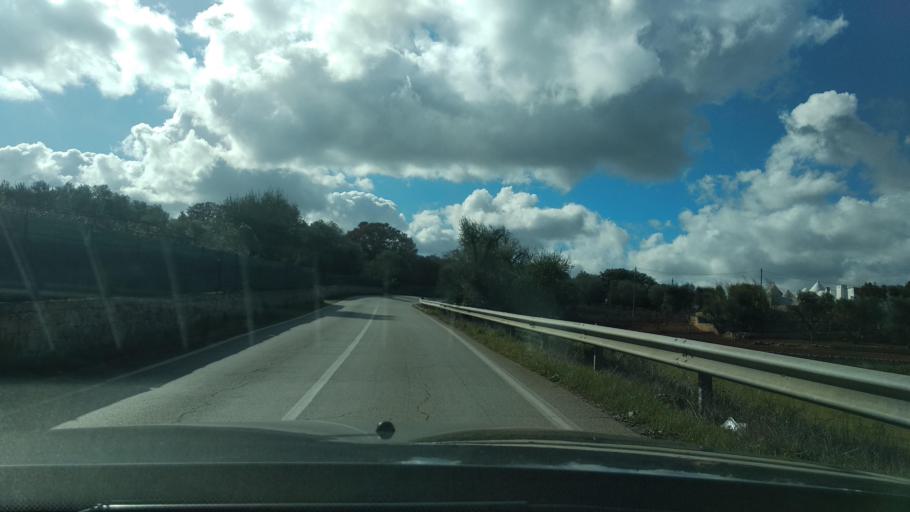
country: IT
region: Apulia
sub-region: Provincia di Brindisi
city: Casalini
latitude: 40.7018
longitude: 17.4962
